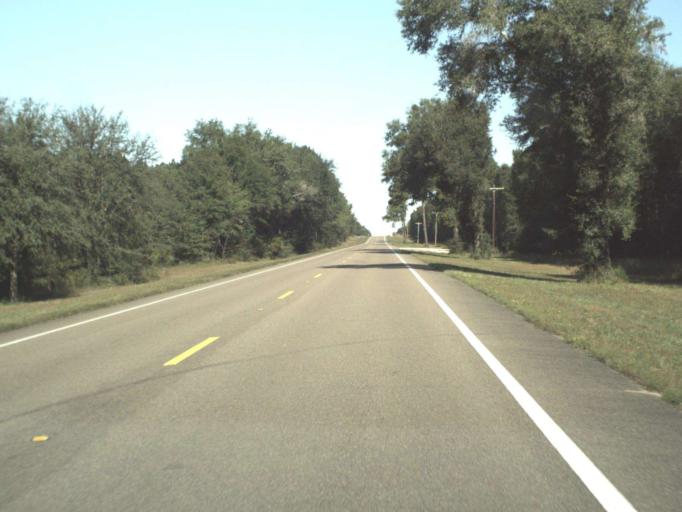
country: US
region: Florida
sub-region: Walton County
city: Freeport
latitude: 30.5567
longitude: -85.9174
